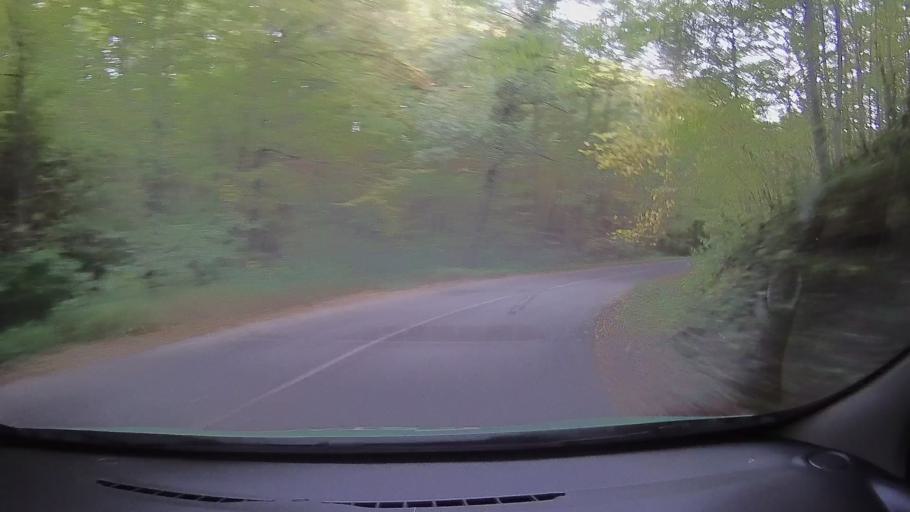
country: RO
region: Timis
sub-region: Comuna Fardea
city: Fardea
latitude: 45.6912
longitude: 22.1567
